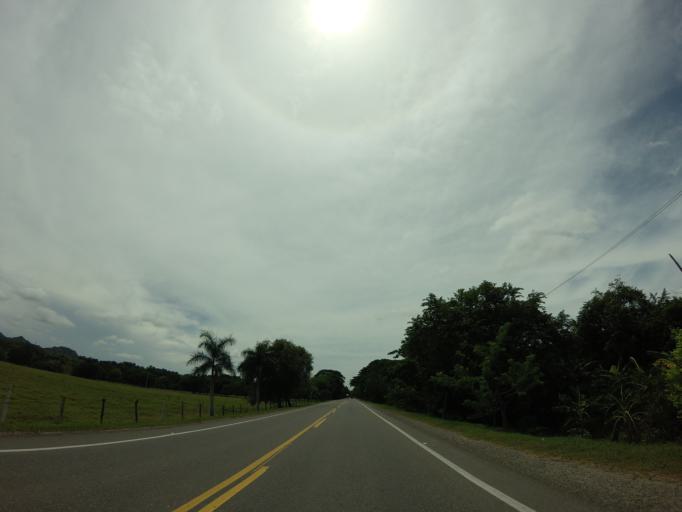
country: CO
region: Caldas
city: La Dorada
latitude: 5.4290
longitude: -74.6815
